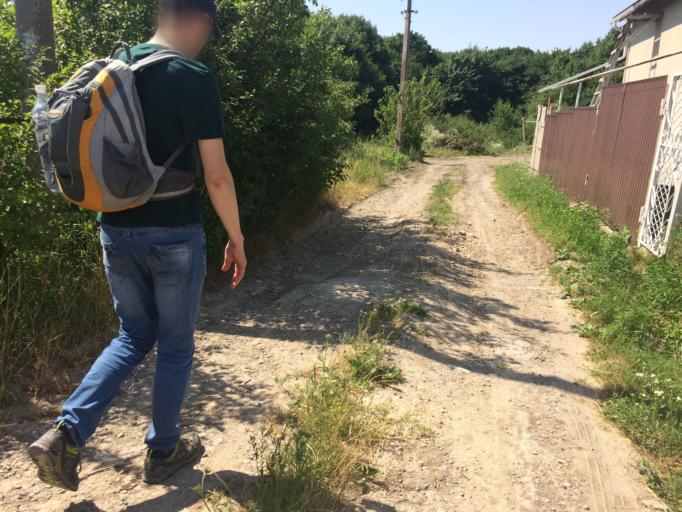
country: RU
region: Stavropol'skiy
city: Tatarka
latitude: 44.9804
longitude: 41.9406
